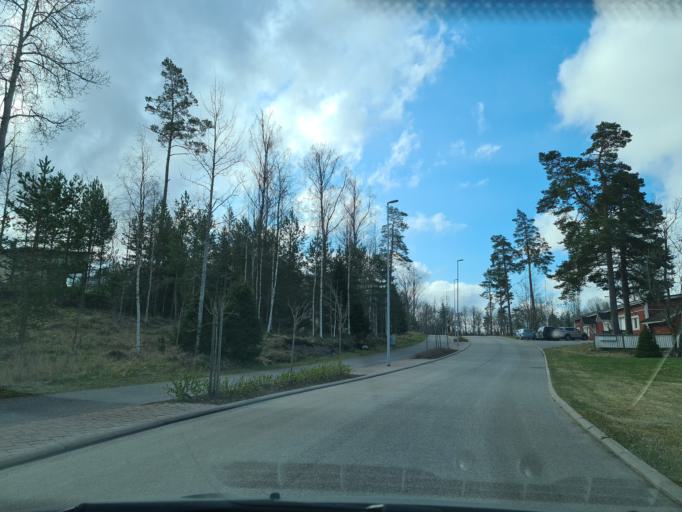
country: FI
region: Uusimaa
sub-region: Helsinki
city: Kirkkonummi
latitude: 60.0799
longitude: 24.4006
